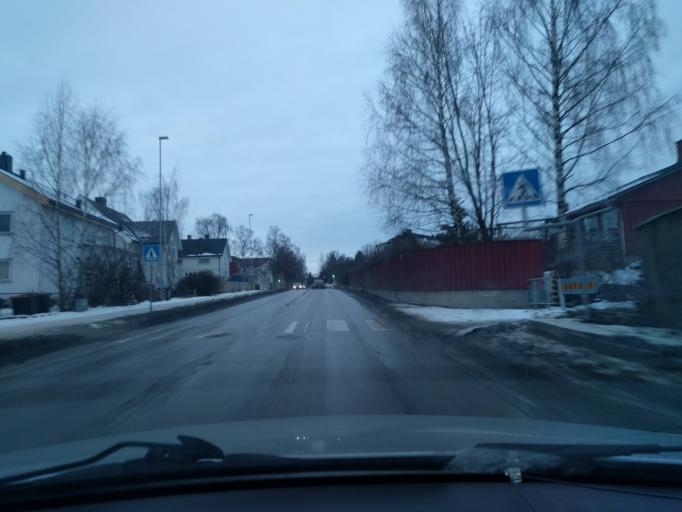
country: NO
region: Hedmark
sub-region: Hamar
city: Hamar
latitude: 60.7993
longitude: 11.0876
